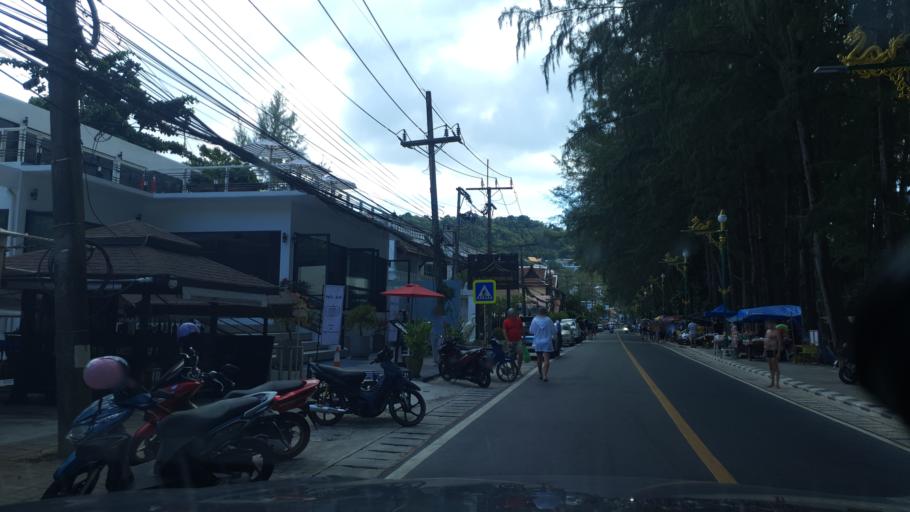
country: TH
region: Phuket
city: Thalang
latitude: 8.0609
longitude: 98.2777
